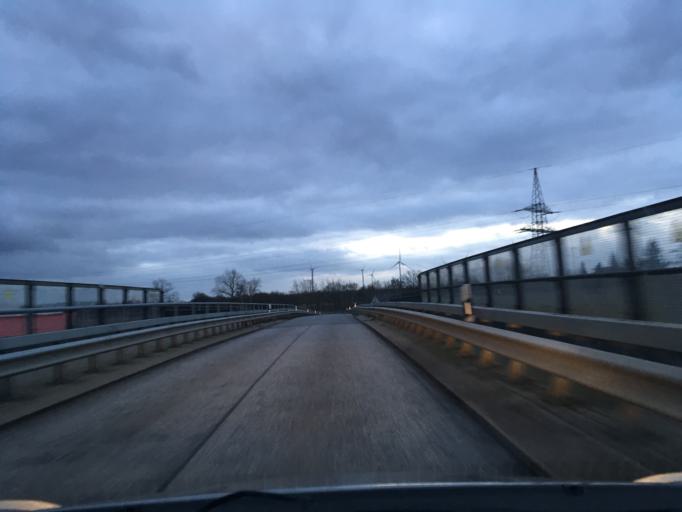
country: DE
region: Lower Saxony
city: Winsen
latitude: 53.3593
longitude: 10.1872
